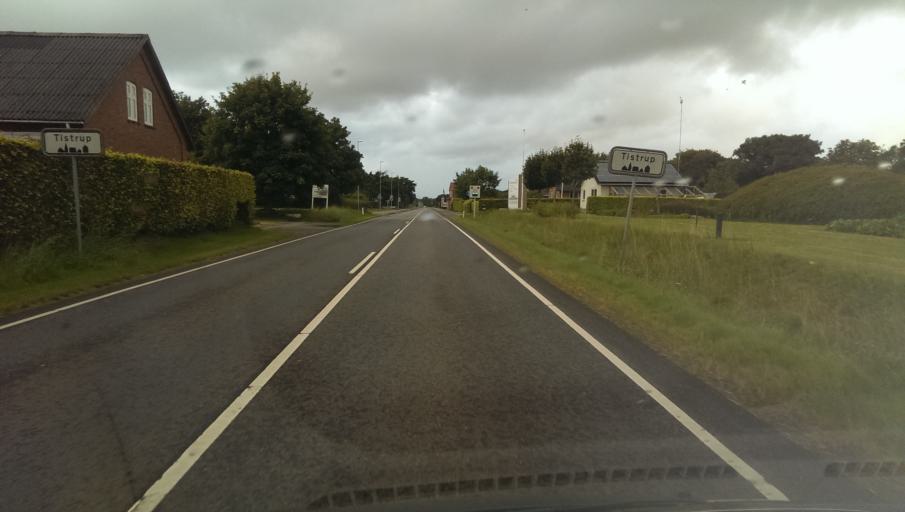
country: DK
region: South Denmark
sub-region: Varde Kommune
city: Olgod
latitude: 55.7145
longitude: 8.6100
